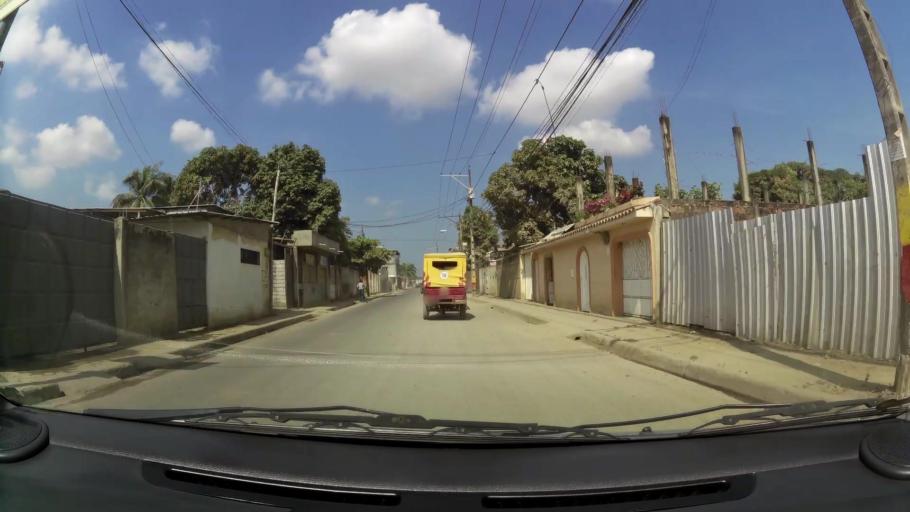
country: EC
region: Guayas
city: Eloy Alfaro
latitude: -2.1660
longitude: -79.8242
